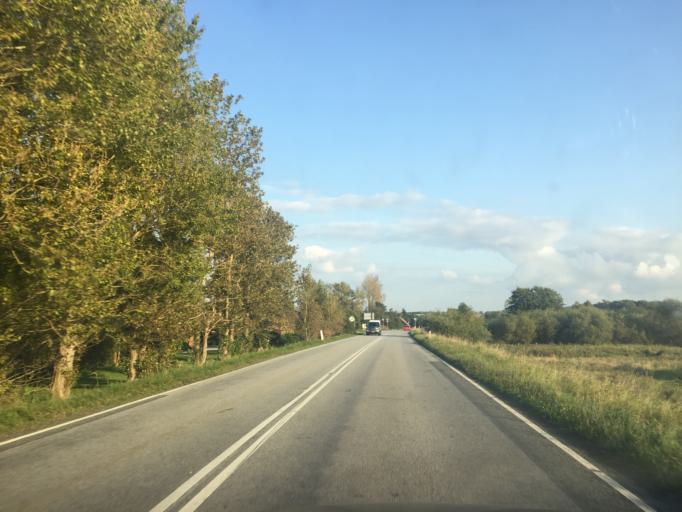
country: DK
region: Zealand
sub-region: Kalundborg Kommune
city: Svebolle
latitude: 55.5960
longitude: 11.3038
